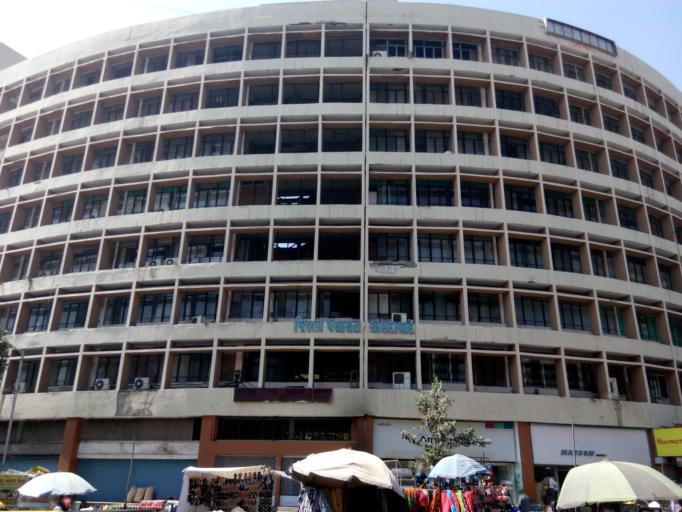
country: IN
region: Gujarat
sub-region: Ahmadabad
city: Ahmedabad
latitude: 23.0245
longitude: 72.5806
